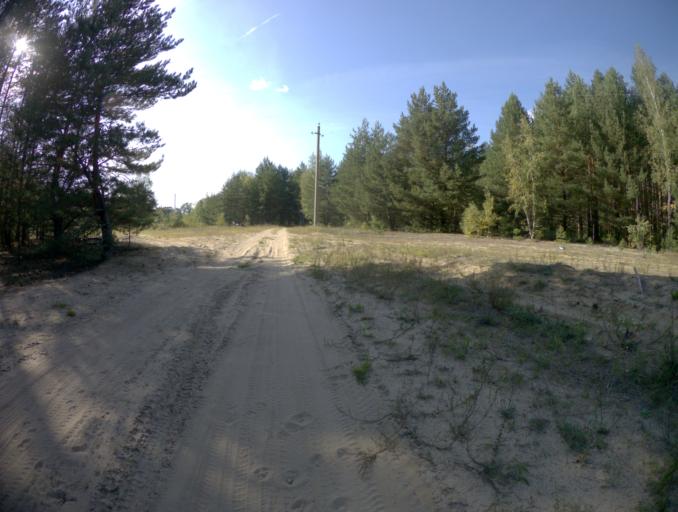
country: RU
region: Vladimir
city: Petushki
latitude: 55.8977
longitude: 39.4604
